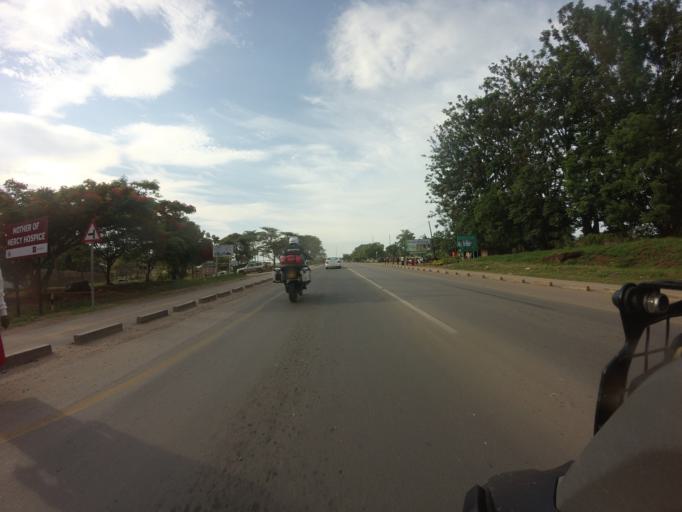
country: ZM
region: Lusaka
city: Lusaka
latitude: -15.5517
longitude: 28.2698
